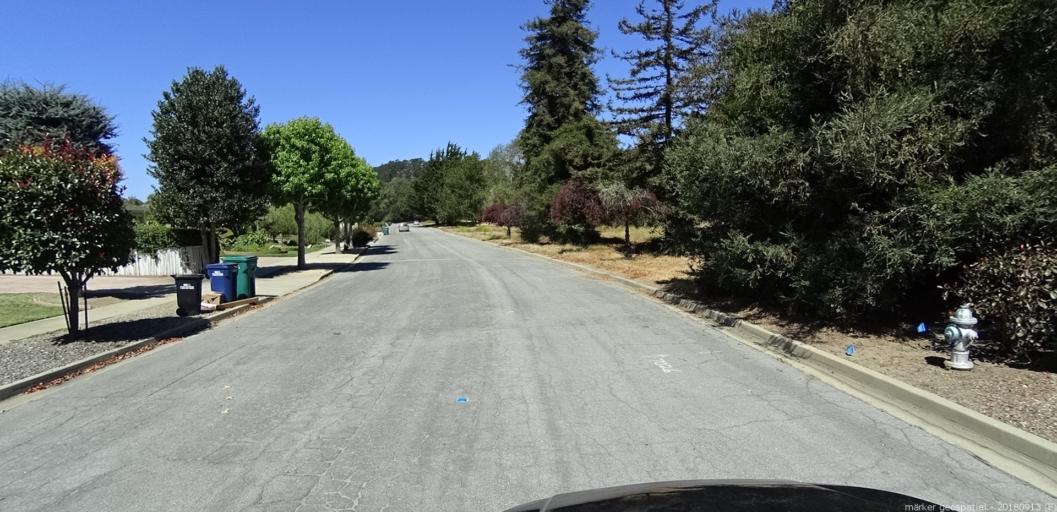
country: US
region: California
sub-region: Monterey County
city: Carmel-by-the-Sea
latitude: 36.5345
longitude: -121.8646
